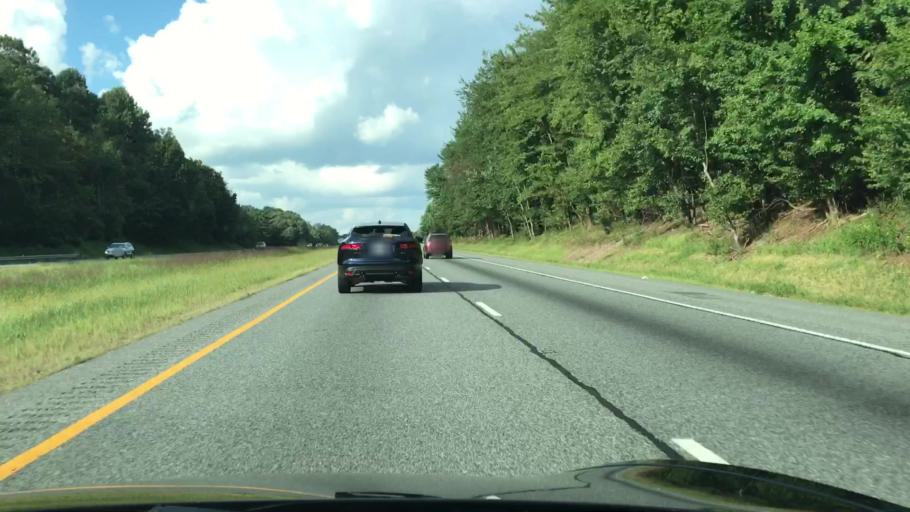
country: US
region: Pennsylvania
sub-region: York County
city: New Freedom
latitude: 39.6716
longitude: -76.6506
